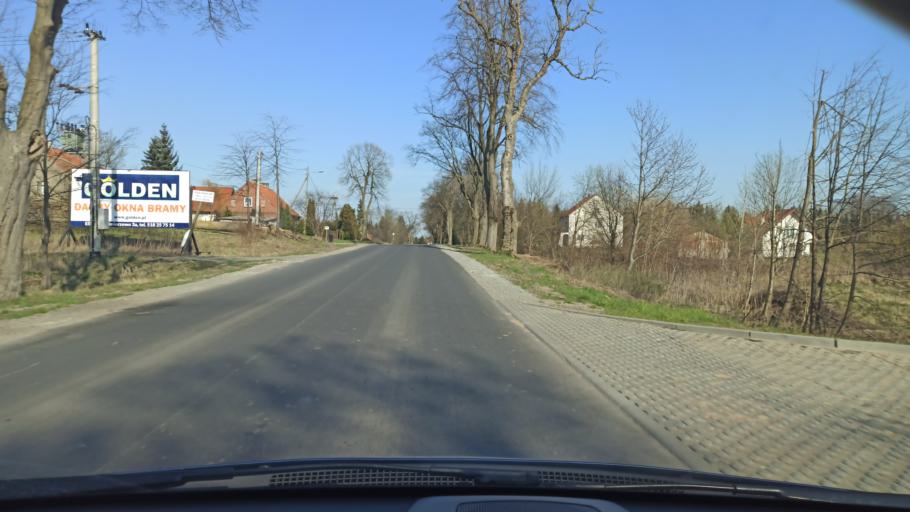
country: PL
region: Warmian-Masurian Voivodeship
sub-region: Powiat elblaski
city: Tolkmicko
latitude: 54.2162
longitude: 19.5317
